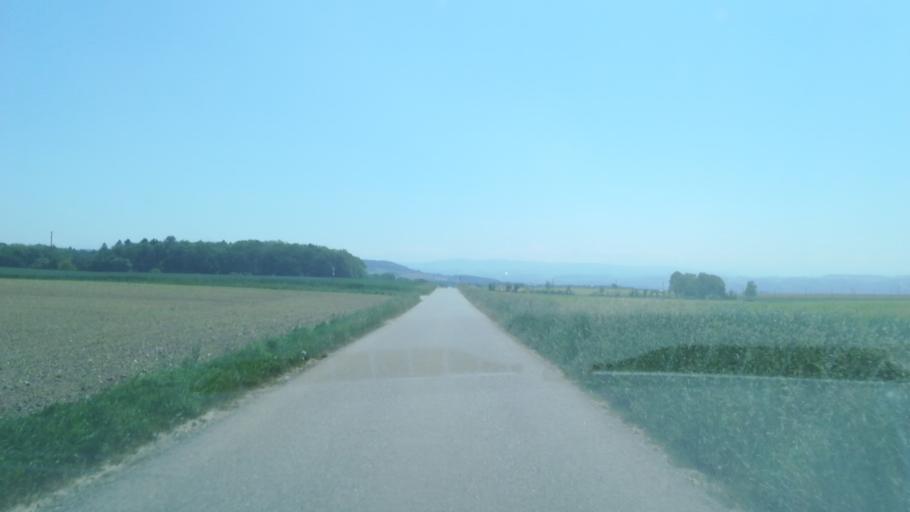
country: CH
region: Thurgau
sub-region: Kreuzlingen District
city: Ermatingen
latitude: 47.6335
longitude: 9.0770
